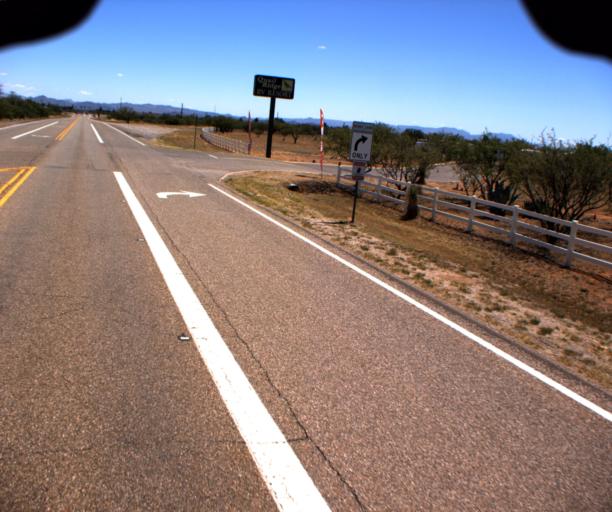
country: US
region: Arizona
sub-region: Cochise County
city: Huachuca City
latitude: 31.6926
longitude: -110.3569
